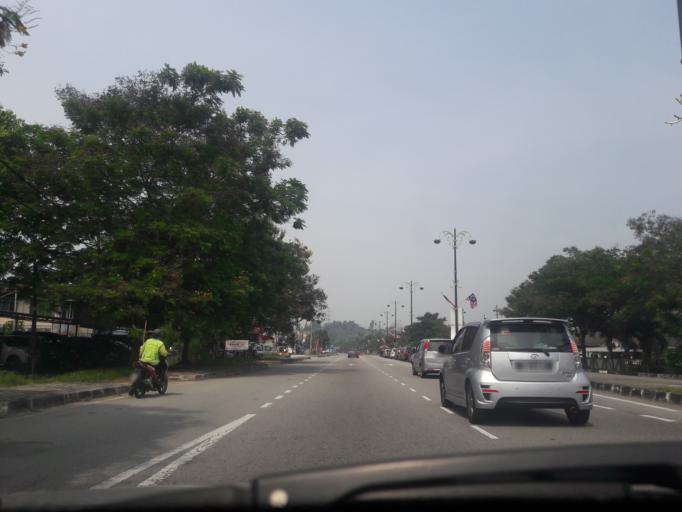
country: MY
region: Kedah
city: Kulim
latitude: 5.3839
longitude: 100.5565
